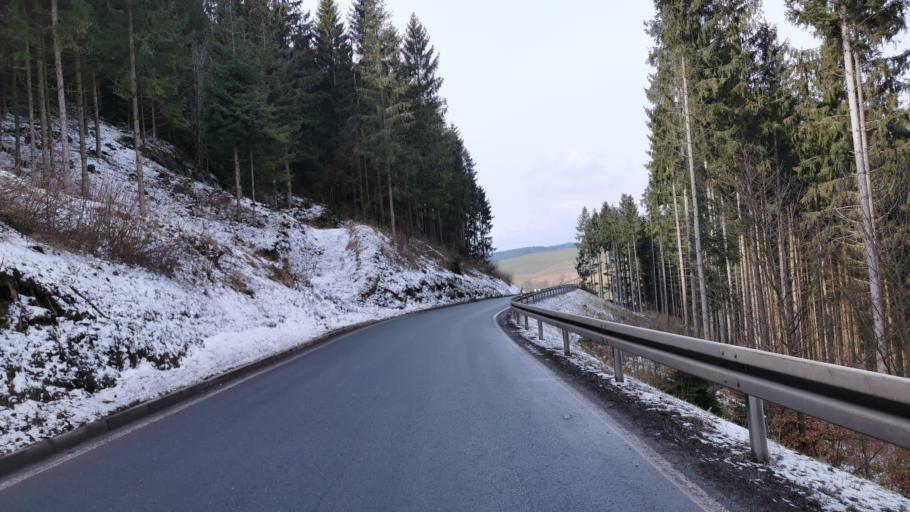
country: DE
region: Bavaria
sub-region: Upper Franconia
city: Ludwigsstadt
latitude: 50.4961
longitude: 11.4032
